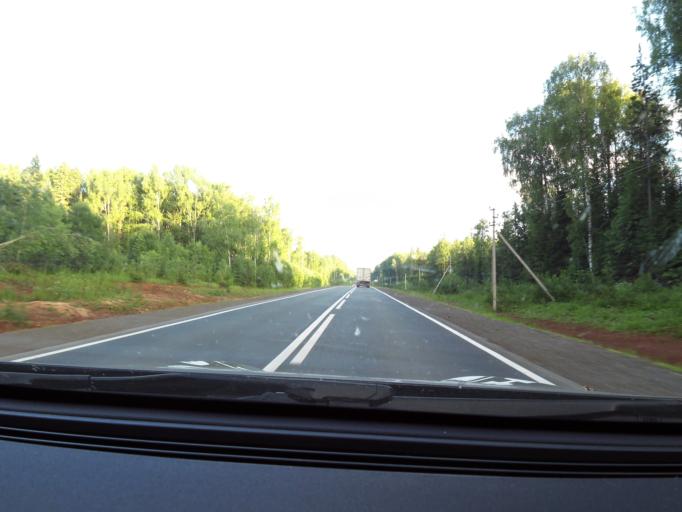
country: RU
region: Perm
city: Siva
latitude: 58.5742
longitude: 53.8867
